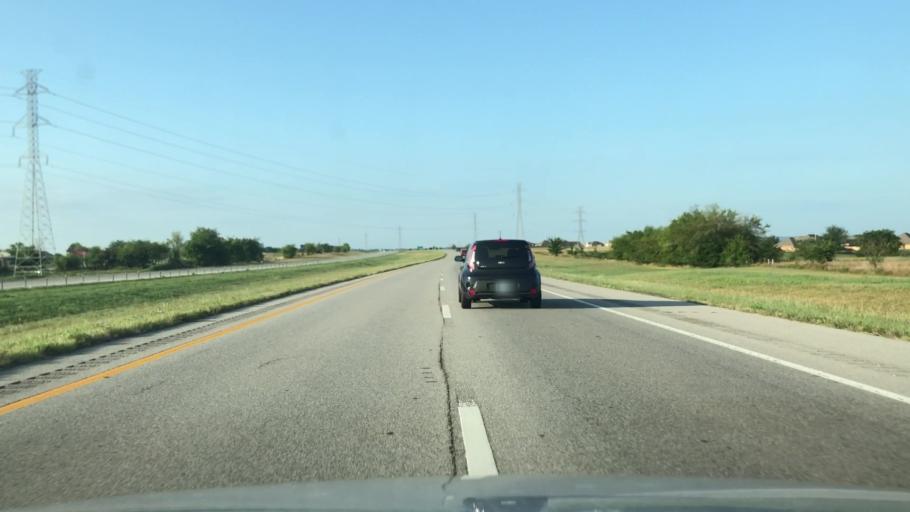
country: US
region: Oklahoma
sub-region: Osage County
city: Skiatook
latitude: 36.3477
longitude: -95.9219
